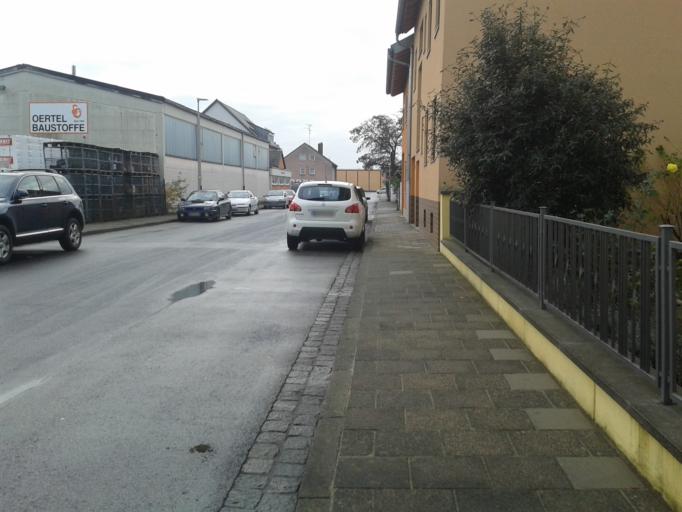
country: DE
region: Bavaria
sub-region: Upper Franconia
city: Hallstadt
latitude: 49.9119
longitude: 10.8820
